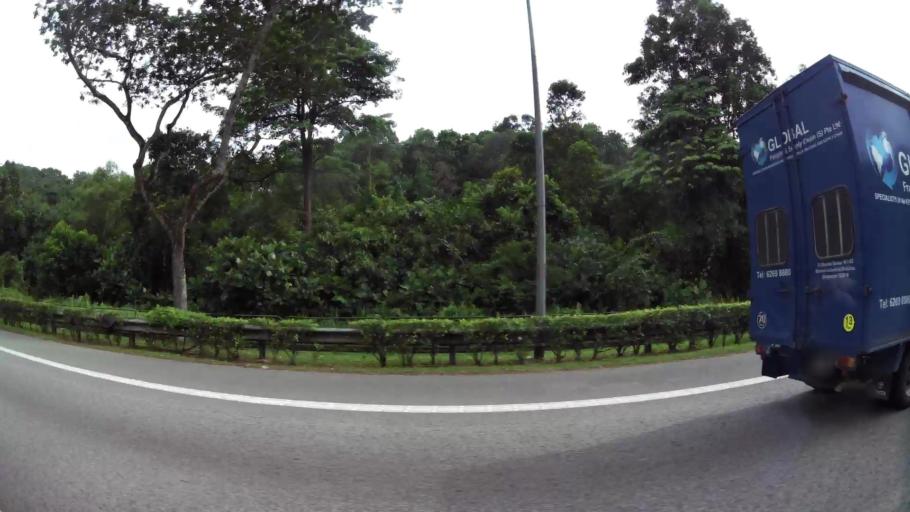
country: MY
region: Johor
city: Johor Bahru
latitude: 1.4261
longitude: 103.7795
